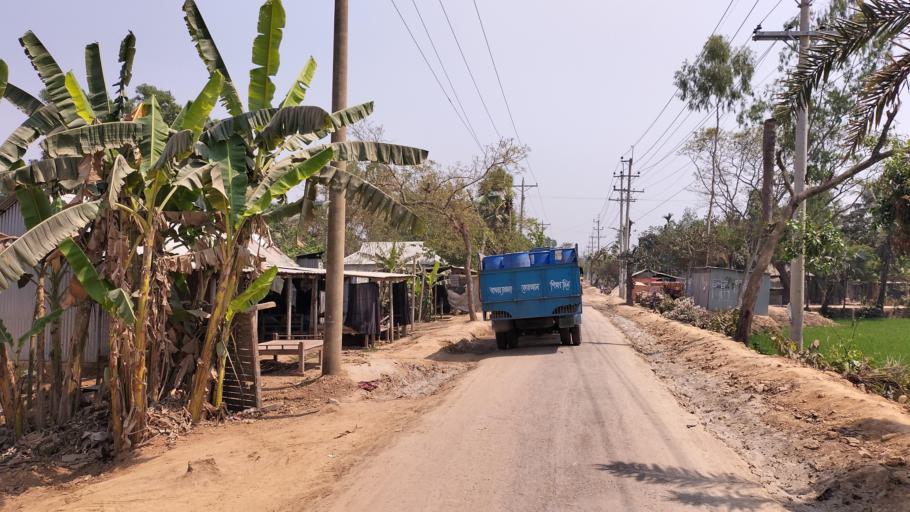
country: BD
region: Dhaka
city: Sakhipur
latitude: 24.3079
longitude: 90.2986
